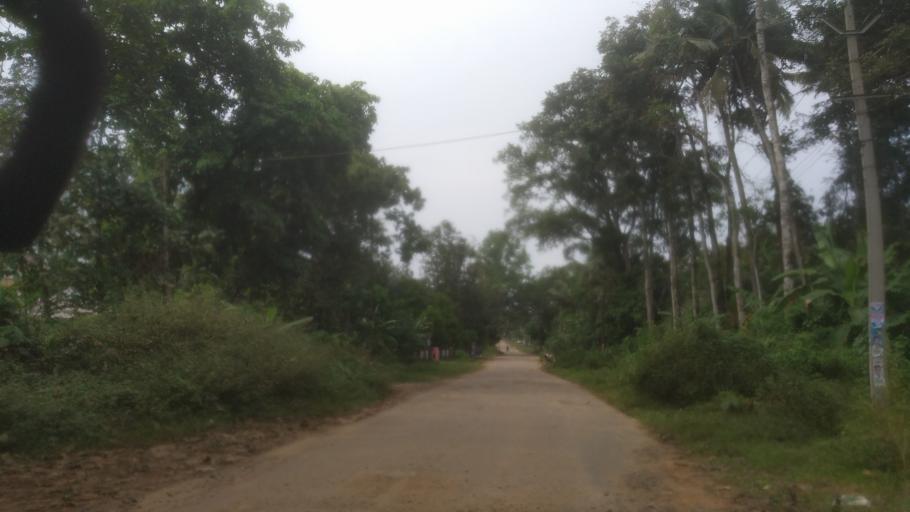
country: IN
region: Kerala
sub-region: Ernakulam
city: Perumbavoor
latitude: 10.0510
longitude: 76.5226
